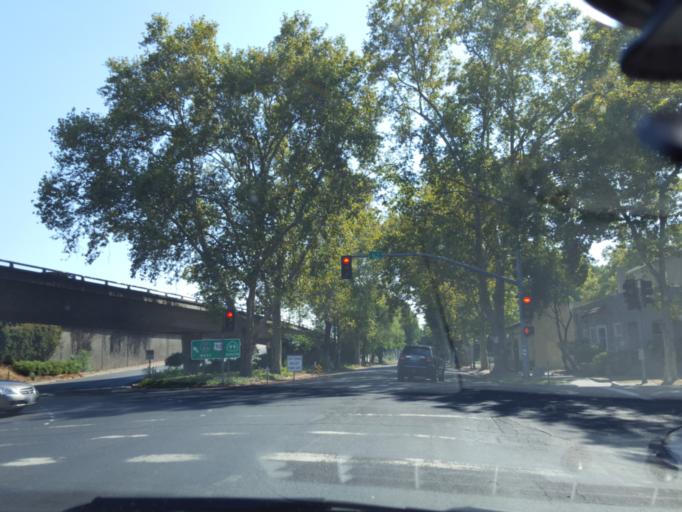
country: US
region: California
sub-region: Sacramento County
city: Sacramento
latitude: 38.5759
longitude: -121.4669
